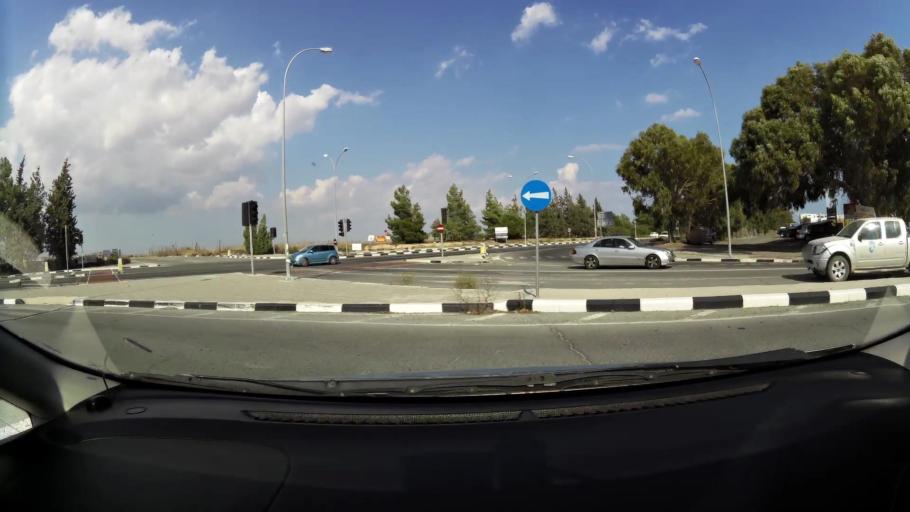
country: CY
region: Larnaka
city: Dhromolaxia
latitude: 34.9081
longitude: 33.5742
